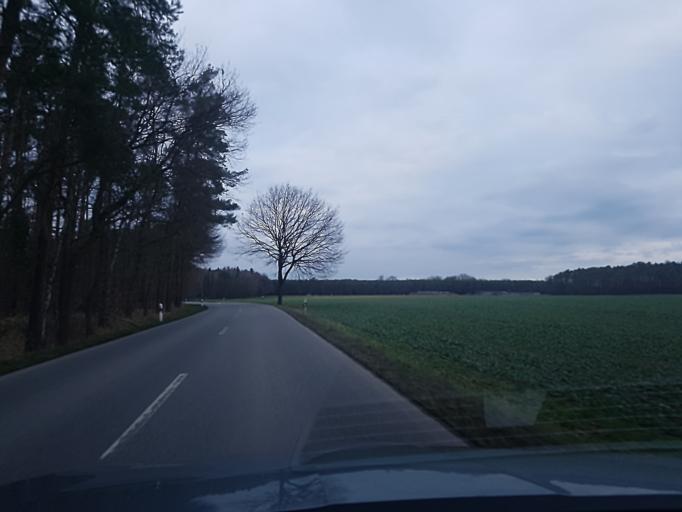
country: DE
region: Brandenburg
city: Finsterwalde
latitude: 51.6728
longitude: 13.6911
